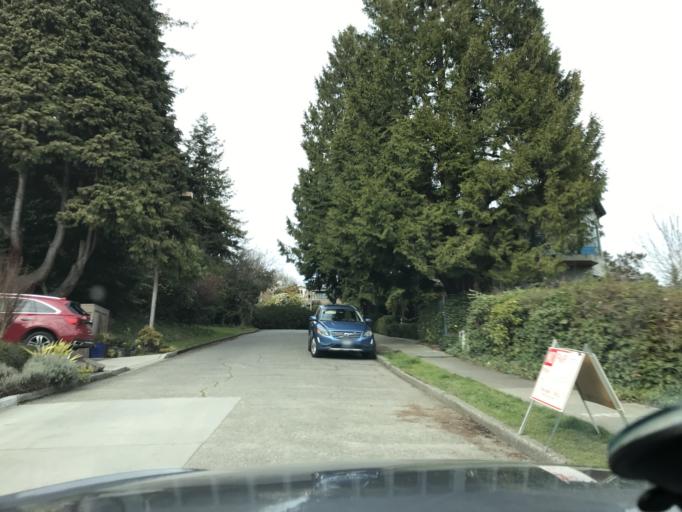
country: US
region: Washington
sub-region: King County
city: Seattle
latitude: 47.6255
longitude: -122.2829
